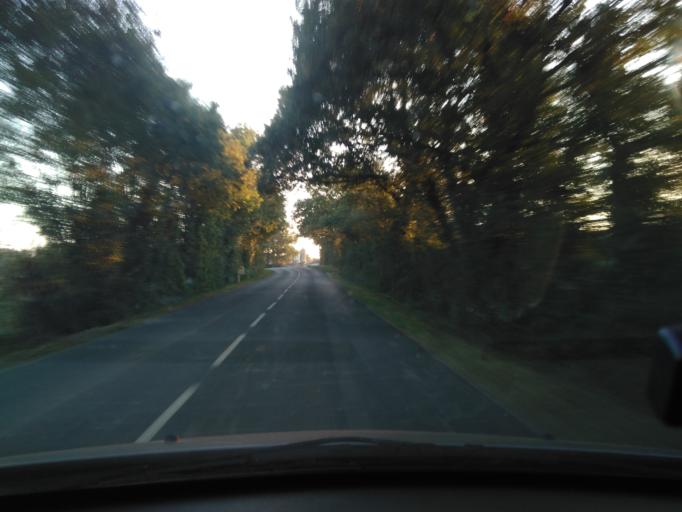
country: FR
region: Pays de la Loire
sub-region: Departement de la Vendee
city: Chauche
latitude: 46.8167
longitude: -1.2666
